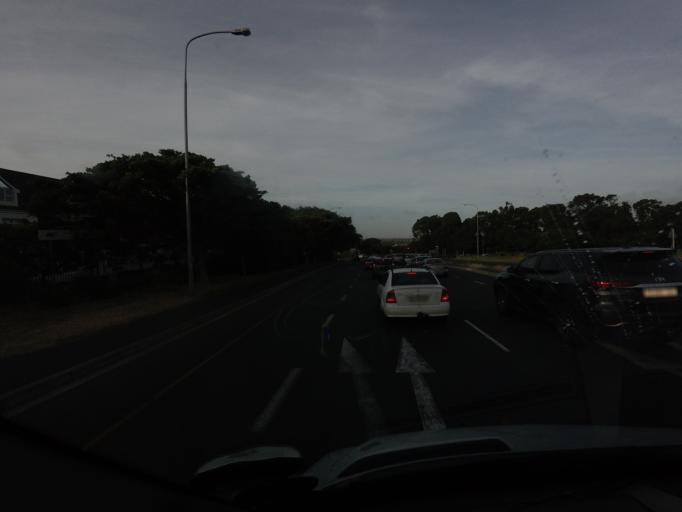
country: ZA
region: Western Cape
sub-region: City of Cape Town
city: Bergvliet
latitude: -34.0813
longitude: 18.4403
